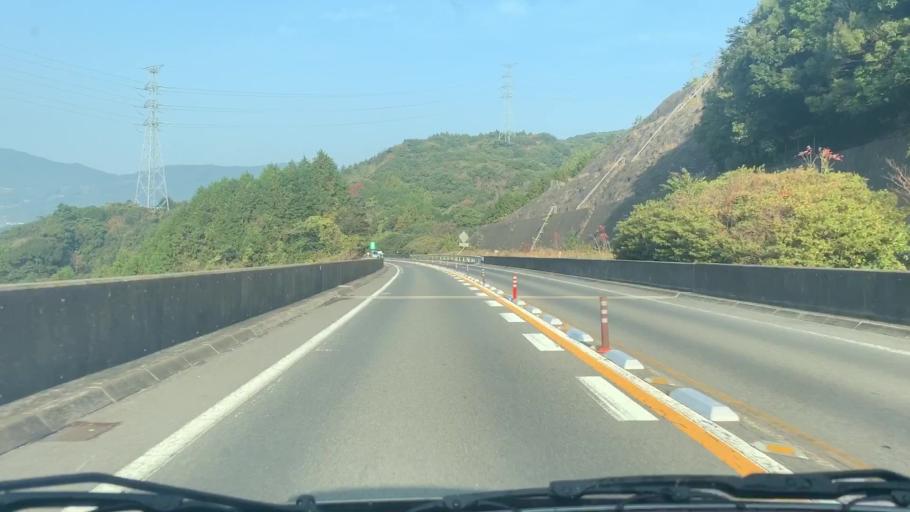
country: JP
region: Saga Prefecture
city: Imaricho-ko
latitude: 33.1641
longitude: 129.8626
